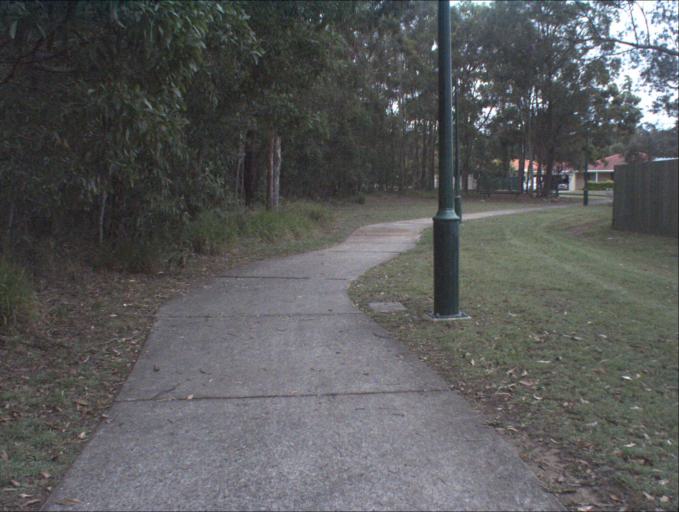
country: AU
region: Queensland
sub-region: Logan
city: Park Ridge South
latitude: -27.6785
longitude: 153.0187
